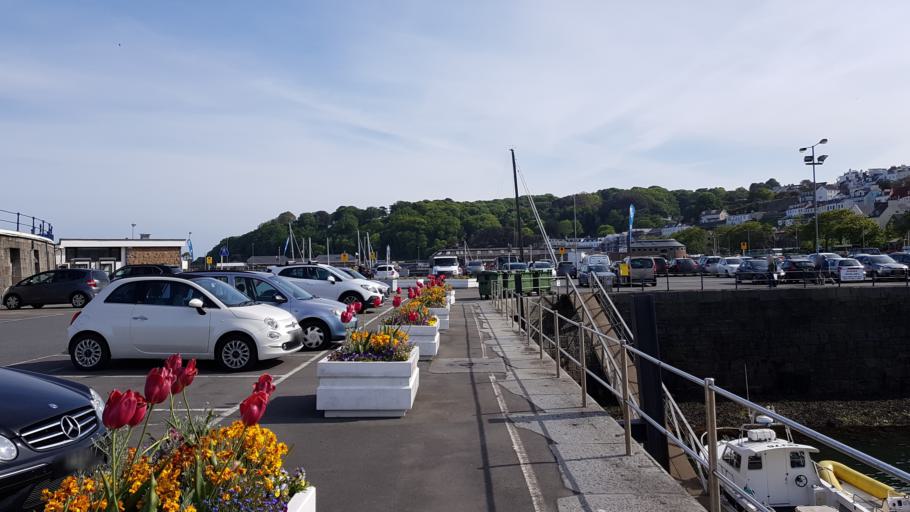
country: GG
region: St Peter Port
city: Saint Peter Port
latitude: 49.4550
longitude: -2.5340
